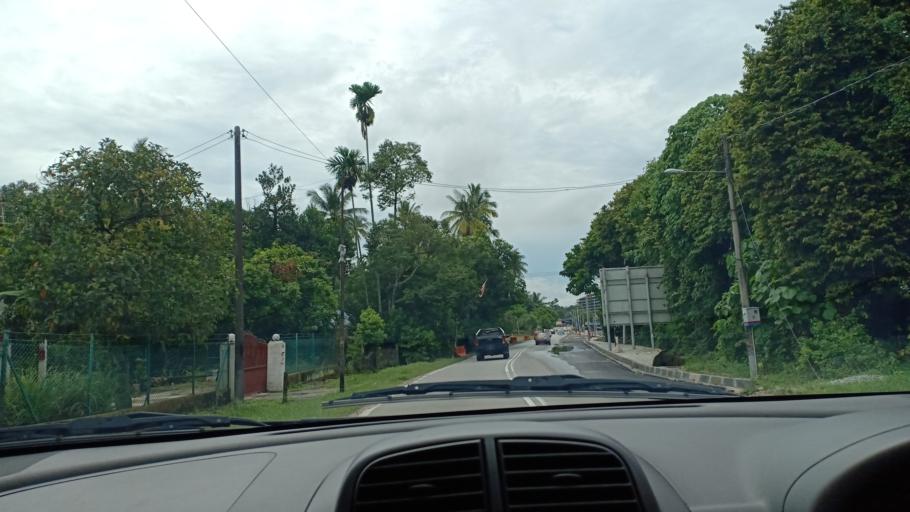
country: MY
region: Penang
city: Bukit Mertajam
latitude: 5.4081
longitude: 100.4802
